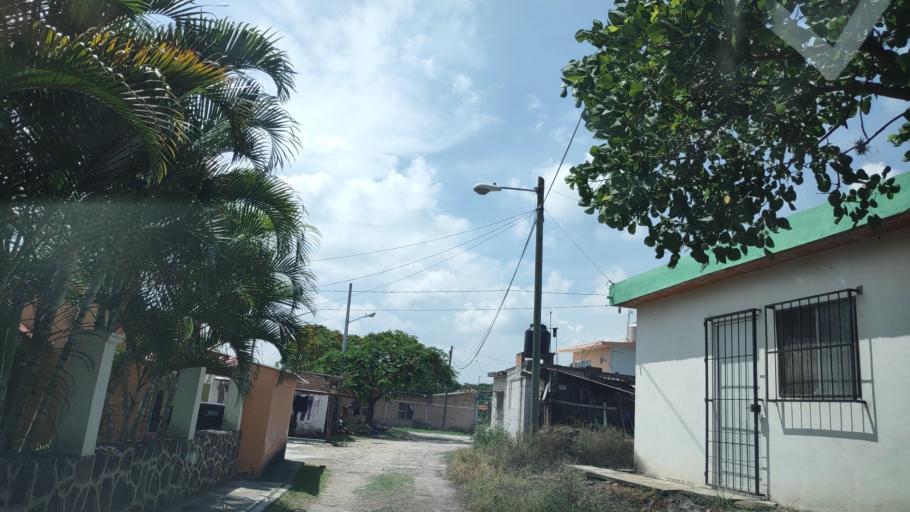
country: MX
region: Veracruz
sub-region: Coatepec
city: Bella Esperanza
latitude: 19.4287
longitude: -96.8107
